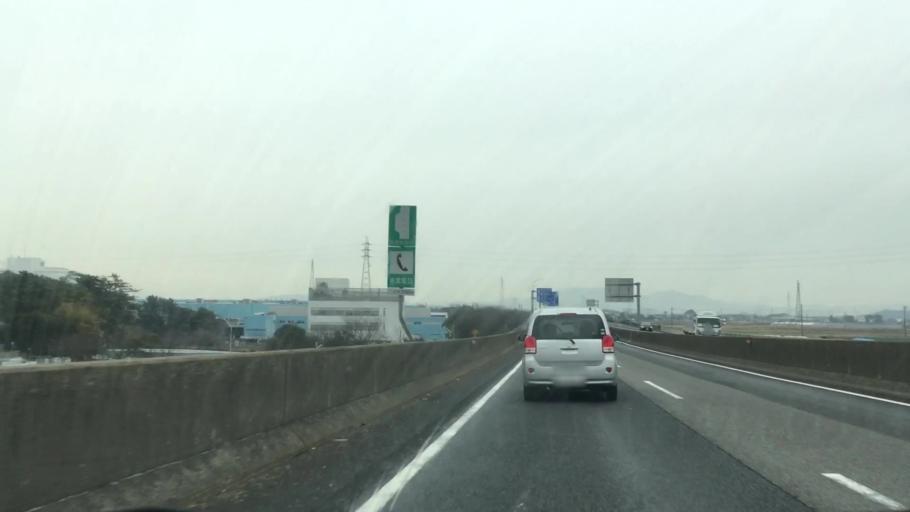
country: JP
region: Aichi
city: Nishio
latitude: 34.9056
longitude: 137.0644
